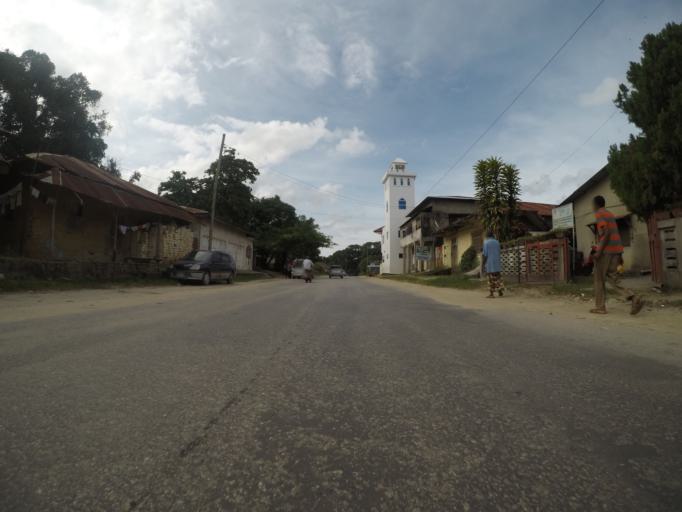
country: TZ
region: Pemba South
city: Chake Chake
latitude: -5.2339
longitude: 39.7769
